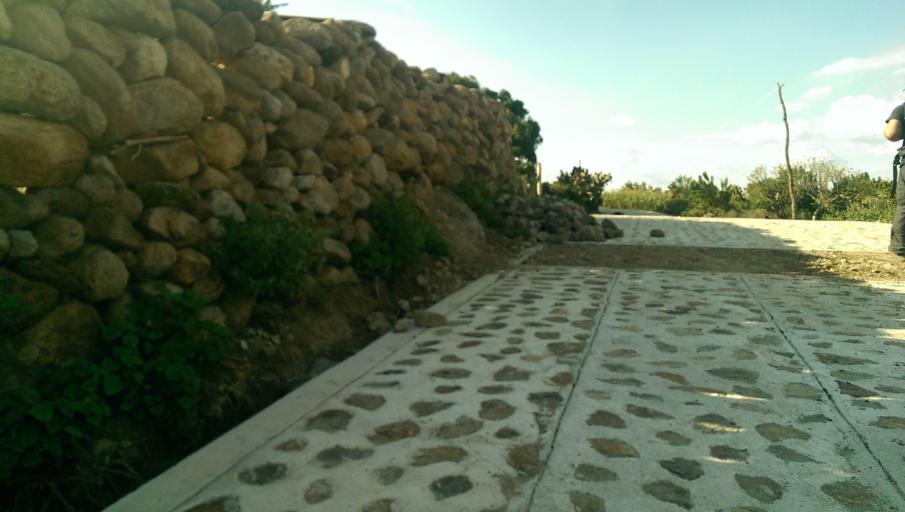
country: MX
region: Queretaro
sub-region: Huimilpan
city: San Jose Tepuzas
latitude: 20.3465
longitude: -100.3741
